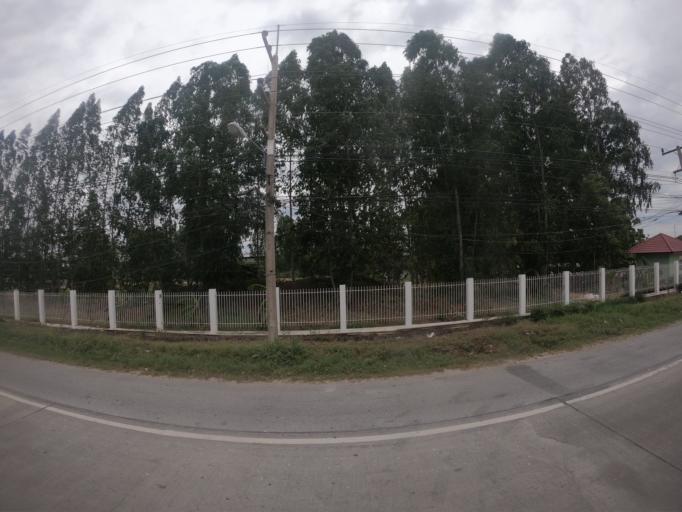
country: TH
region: Nakhon Ratchasima
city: Chok Chai
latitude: 14.8018
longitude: 102.1720
